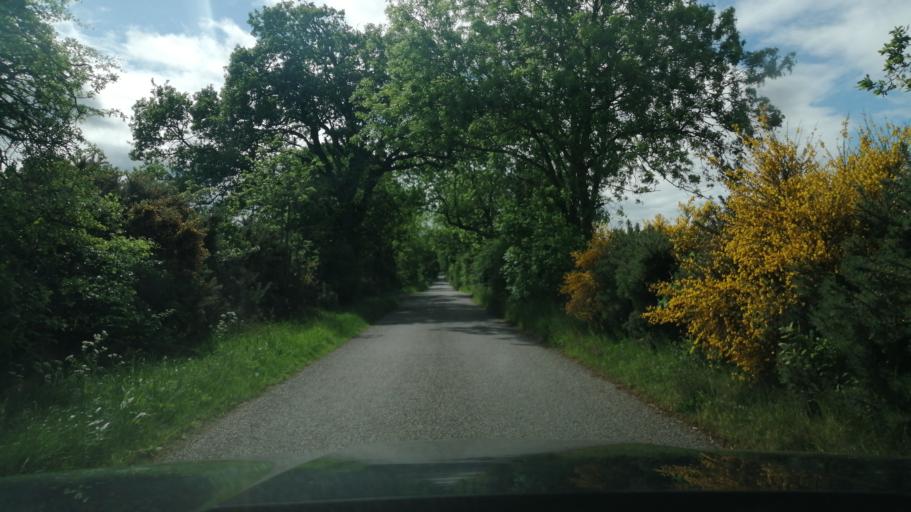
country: GB
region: Scotland
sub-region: Moray
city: Lhanbryd
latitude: 57.6544
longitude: -3.2683
